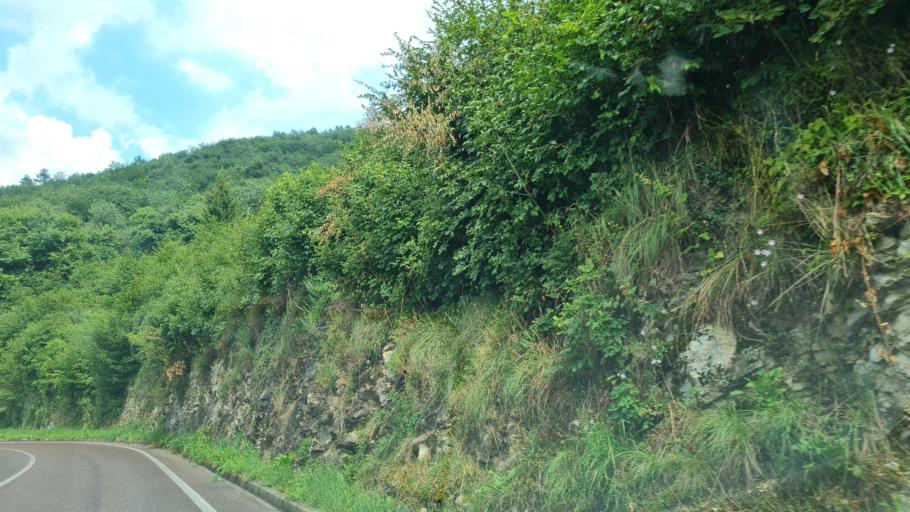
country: IT
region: Veneto
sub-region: Provincia di Vicenza
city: Marostica
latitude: 45.7900
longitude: 11.6543
